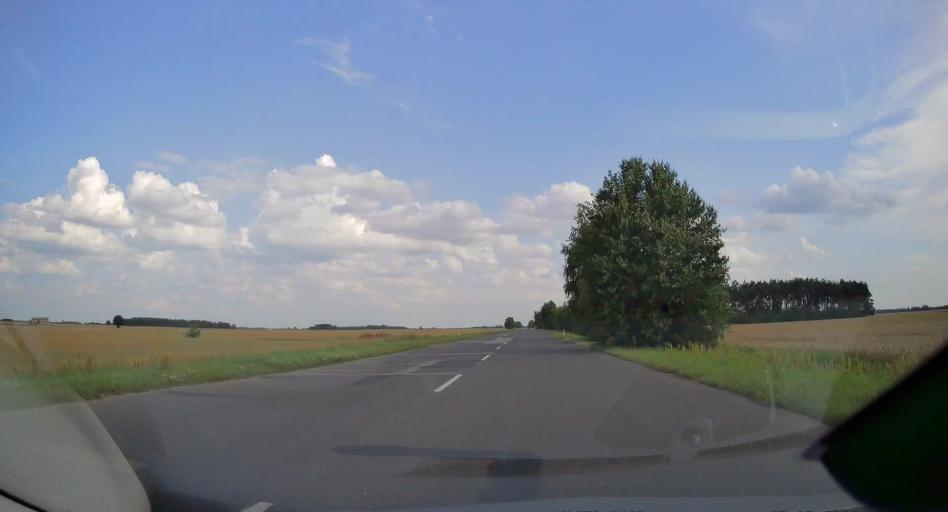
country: PL
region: Lodz Voivodeship
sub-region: Powiat tomaszowski
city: Rzeczyca
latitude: 51.6624
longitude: 20.2685
